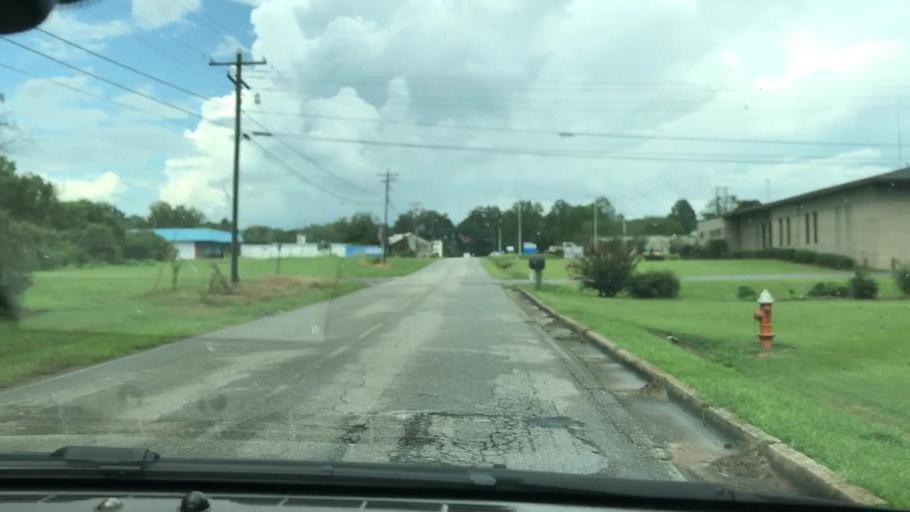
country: US
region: Georgia
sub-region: Early County
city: Blakely
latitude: 31.3705
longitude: -84.9470
